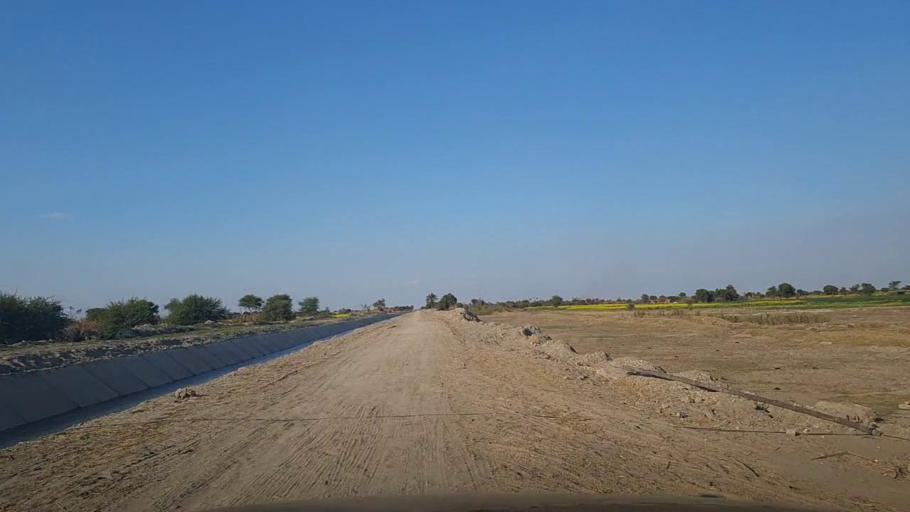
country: PK
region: Sindh
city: Jhol
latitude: 25.9006
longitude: 69.0391
